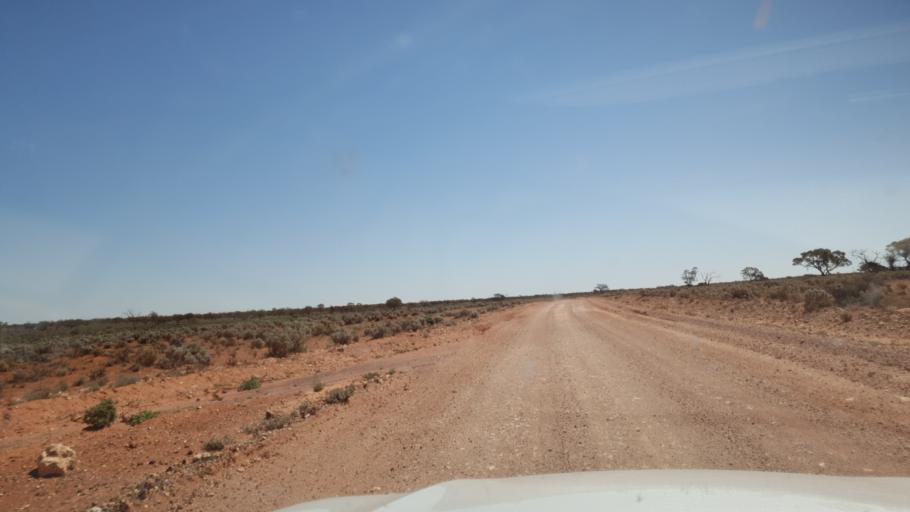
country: AU
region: South Australia
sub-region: Whyalla
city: Whyalla
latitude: -32.6569
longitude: 137.0423
